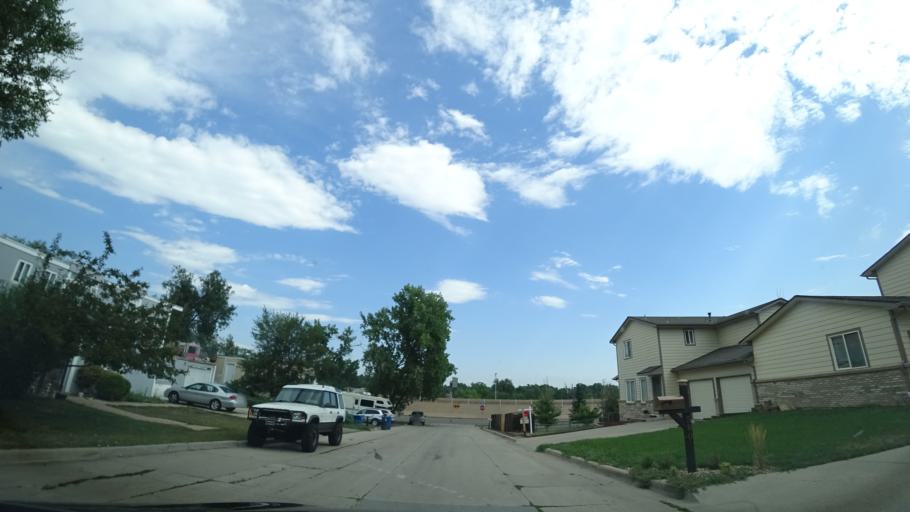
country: US
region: Colorado
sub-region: Jefferson County
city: Lakewood
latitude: 39.7247
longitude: -105.0639
